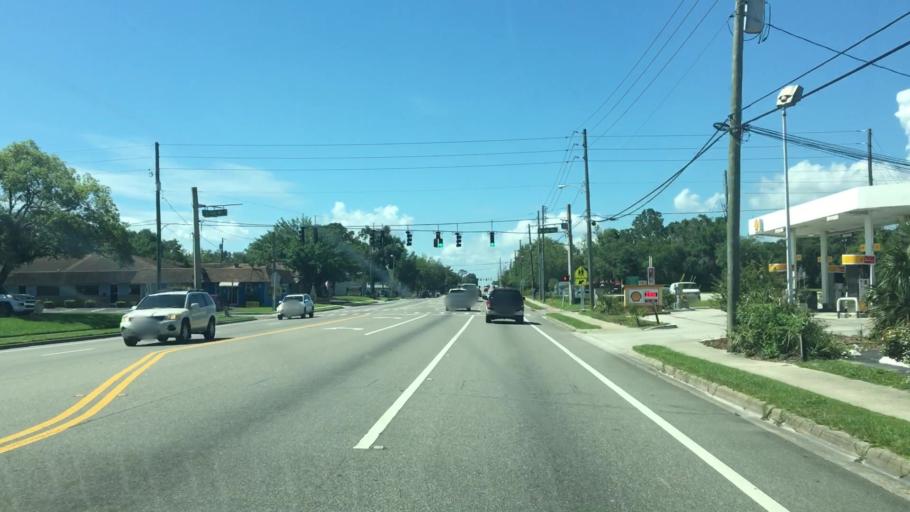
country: US
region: Florida
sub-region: Volusia County
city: Orange City
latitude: 28.9401
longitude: -81.2990
